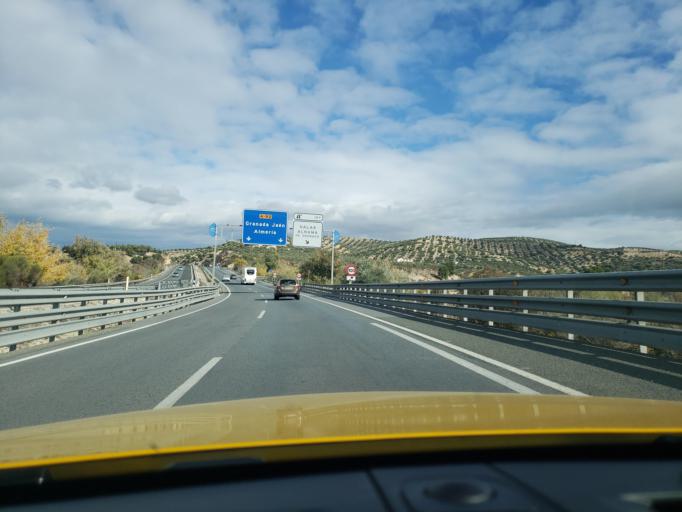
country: ES
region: Andalusia
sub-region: Provincia de Granada
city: Salar
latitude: 37.1673
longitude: -4.0874
